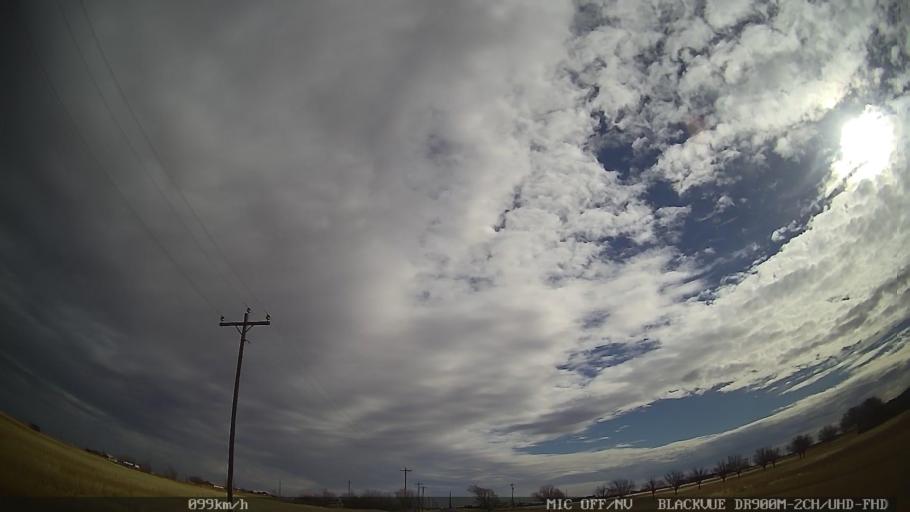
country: US
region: New Mexico
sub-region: Curry County
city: Clovis
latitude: 34.4194
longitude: -103.1527
